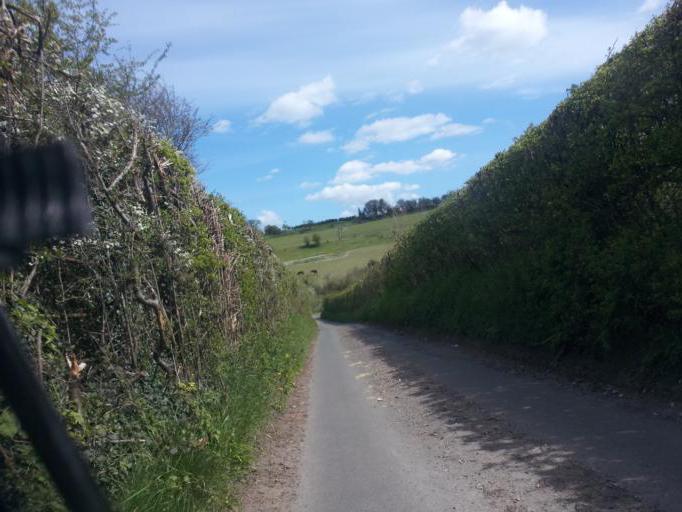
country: GB
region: England
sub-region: Kent
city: Rainham
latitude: 51.3296
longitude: 0.6091
